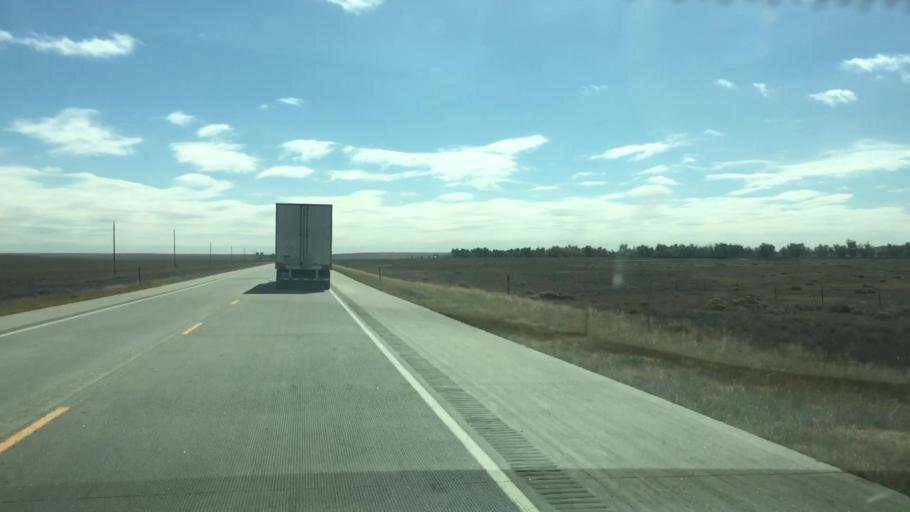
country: US
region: Colorado
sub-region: Lincoln County
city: Hugo
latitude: 39.0668
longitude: -103.3701
